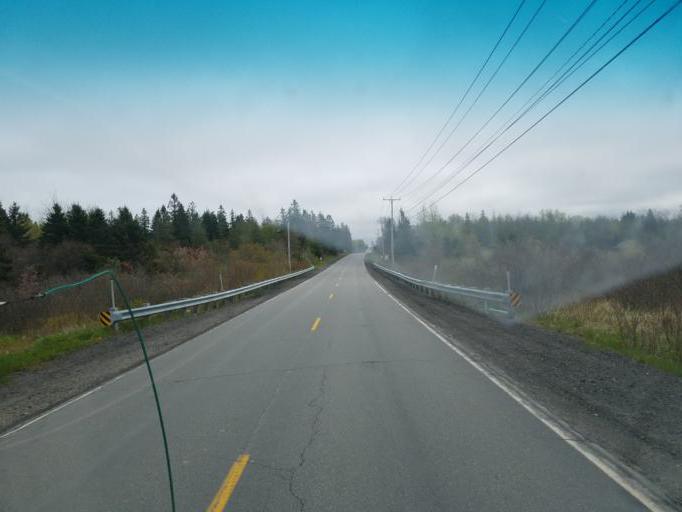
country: US
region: Maine
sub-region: Washington County
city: Eastport
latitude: 44.8296
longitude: -67.0382
